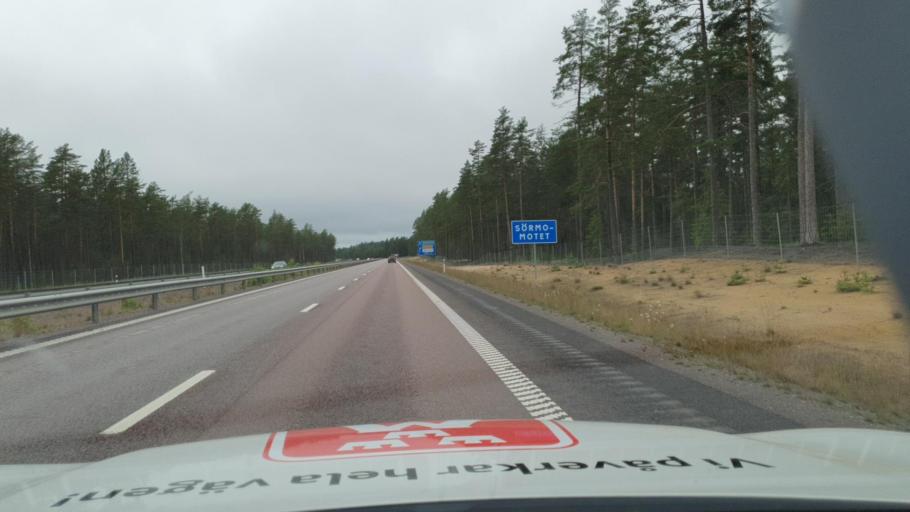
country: SE
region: Vaermland
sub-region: Hammaro Kommun
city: Skoghall
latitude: 59.3838
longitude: 13.3591
